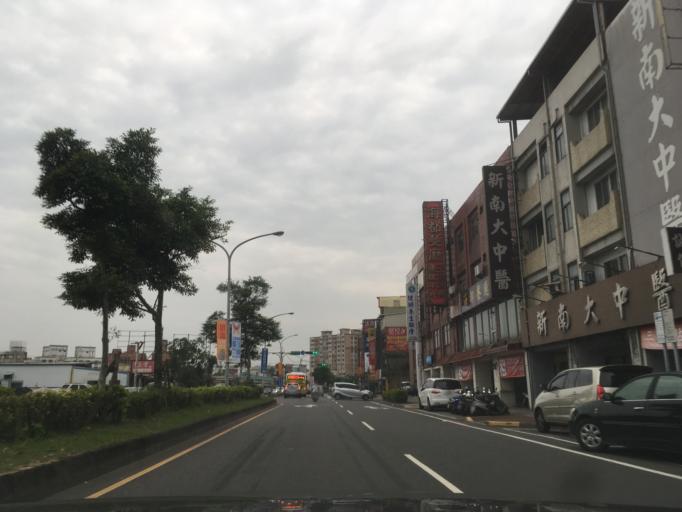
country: TW
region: Taiwan
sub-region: Yilan
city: Yilan
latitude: 24.7512
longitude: 121.7562
